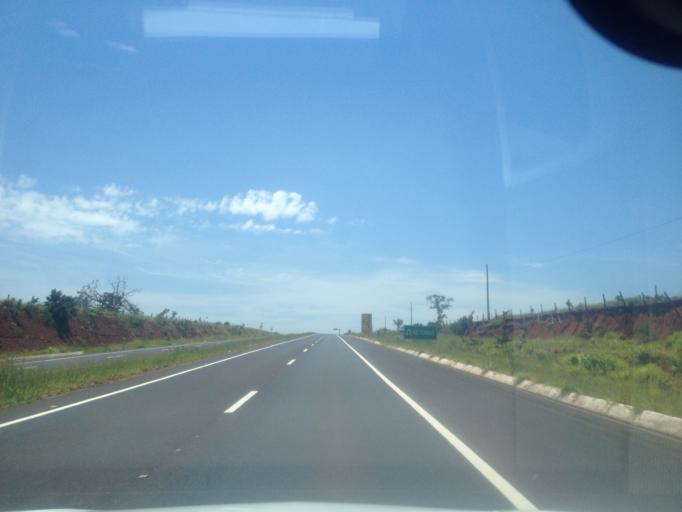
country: BR
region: Minas Gerais
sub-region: Monte Alegre De Minas
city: Monte Alegre de Minas
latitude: -18.8827
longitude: -49.0263
